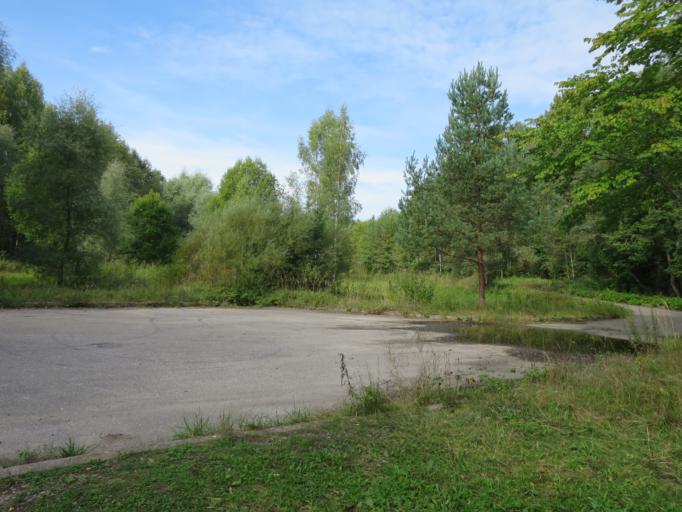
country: LV
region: Sigulda
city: Sigulda
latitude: 57.1784
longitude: 24.8241
